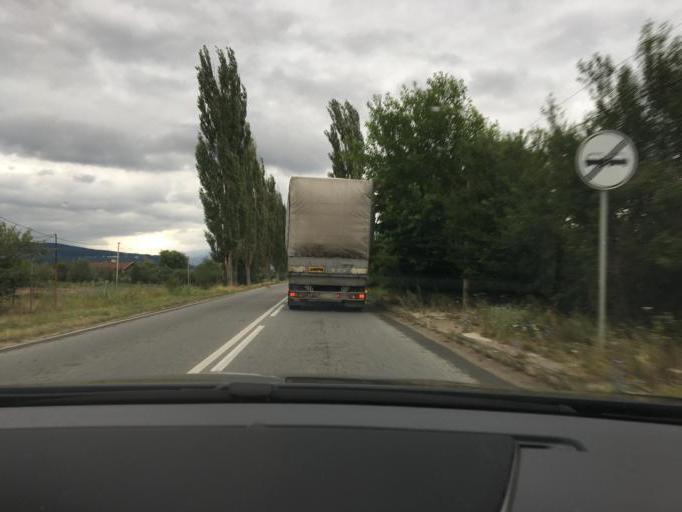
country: BG
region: Kyustendil
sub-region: Obshtina Kyustendil
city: Kyustendil
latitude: 42.2752
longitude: 22.7547
